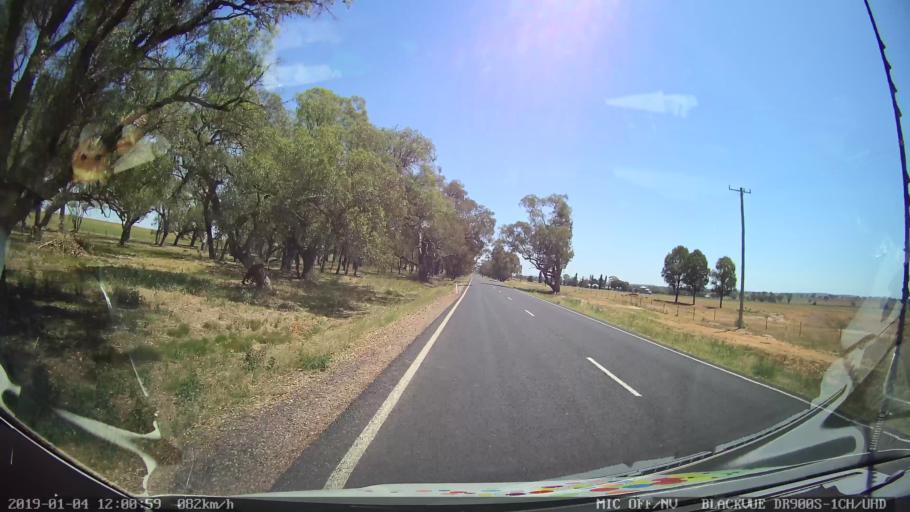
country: AU
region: New South Wales
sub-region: Cabonne
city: Molong
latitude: -32.7963
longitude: 148.6895
